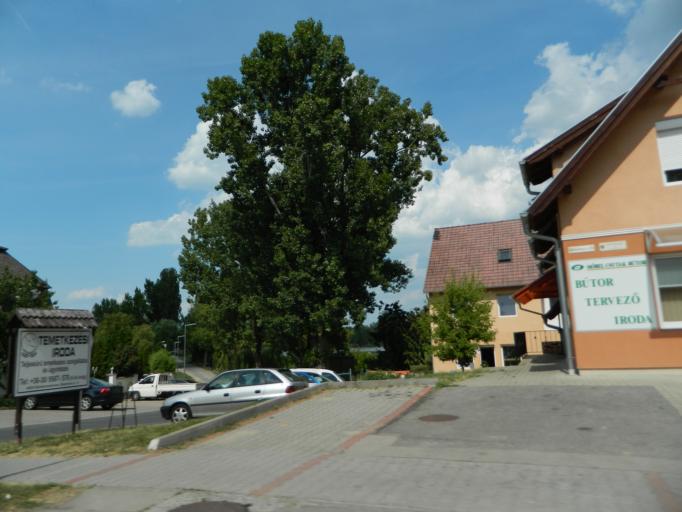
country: HU
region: Somogy
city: Balatonfoldvar
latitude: 46.8477
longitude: 17.8806
